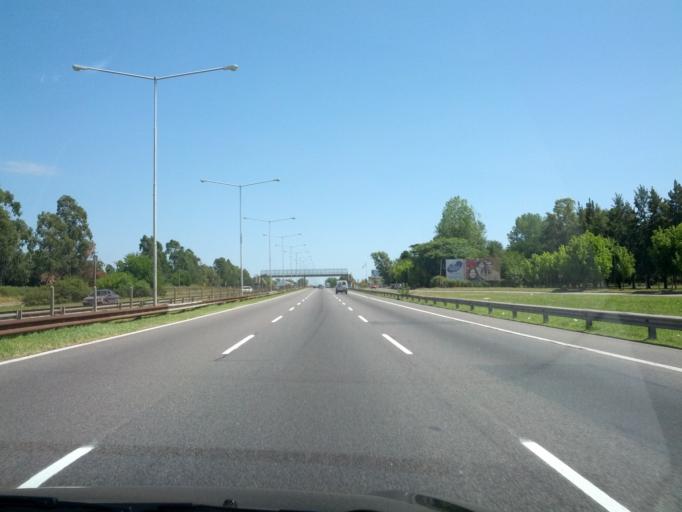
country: AR
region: Buenos Aires
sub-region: Partido de Campana
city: Campana
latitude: -34.2157
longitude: -58.9259
